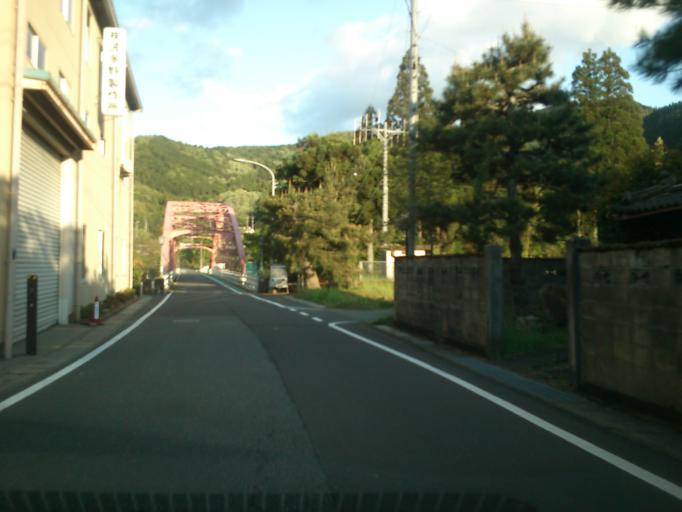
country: JP
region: Kyoto
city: Ayabe
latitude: 35.2946
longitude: 135.3152
